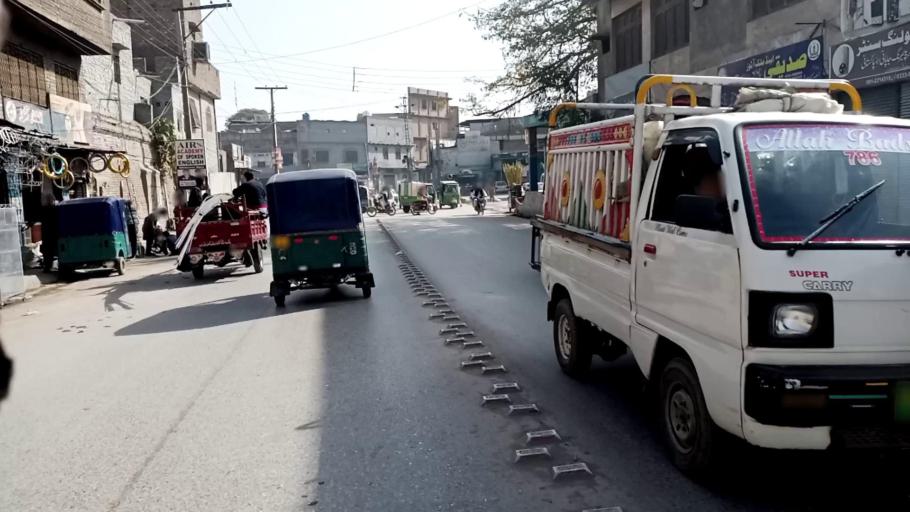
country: PK
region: Khyber Pakhtunkhwa
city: Peshawar
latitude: 34.0051
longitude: 71.5834
